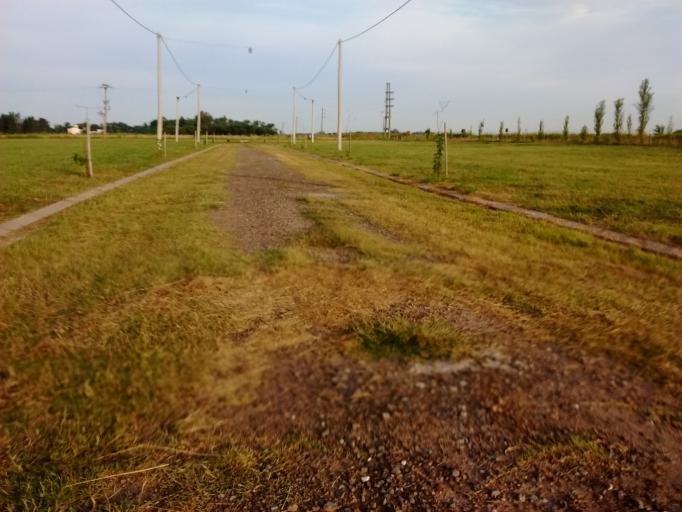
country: AR
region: Santa Fe
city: Roldan
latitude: -32.9295
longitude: -60.8734
